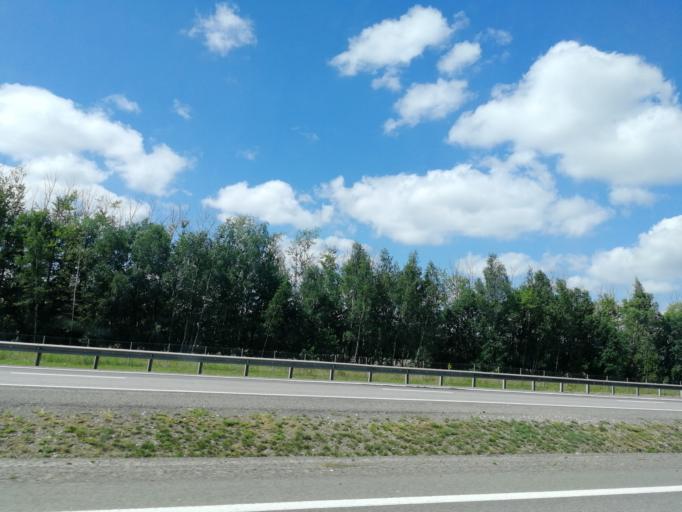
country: RU
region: Tula
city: Dubovka
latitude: 53.9075
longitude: 38.0478
